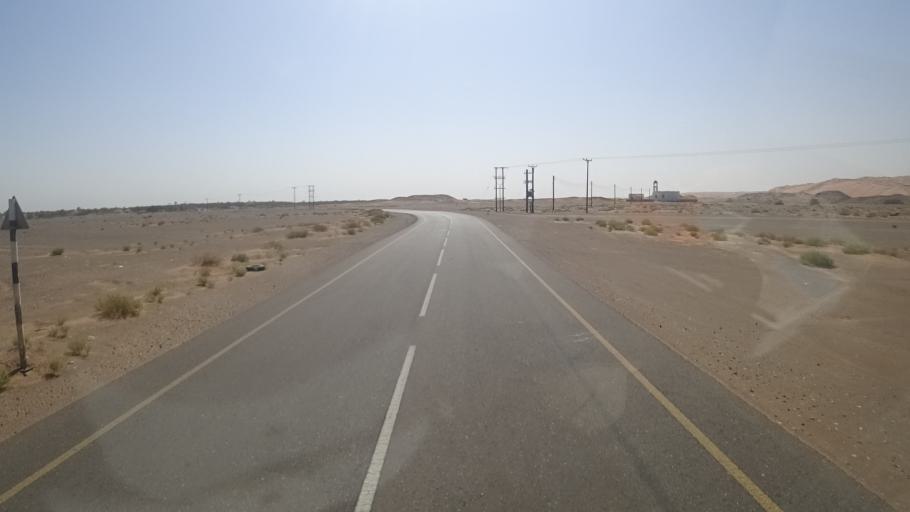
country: OM
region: Ash Sharqiyah
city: Al Qabil
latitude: 22.4985
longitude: 58.7297
